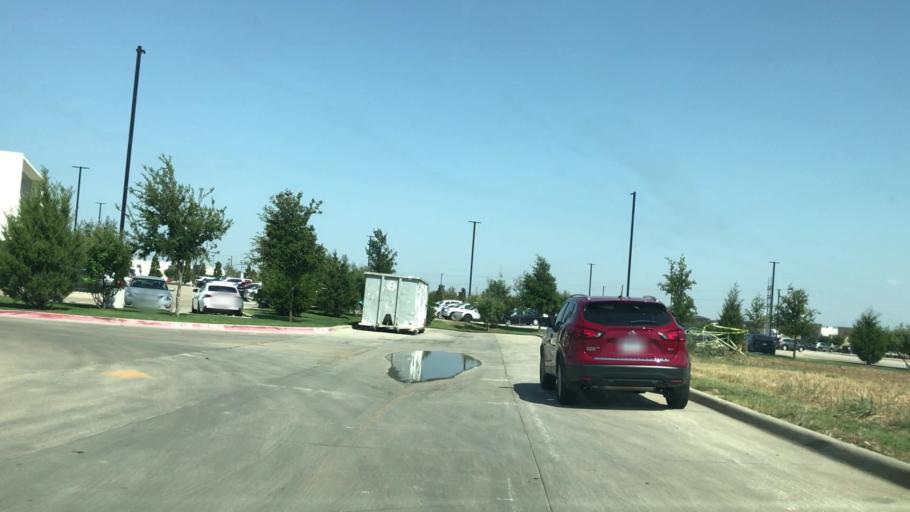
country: US
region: Texas
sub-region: Dallas County
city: Coppell
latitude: 32.9241
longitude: -96.9893
